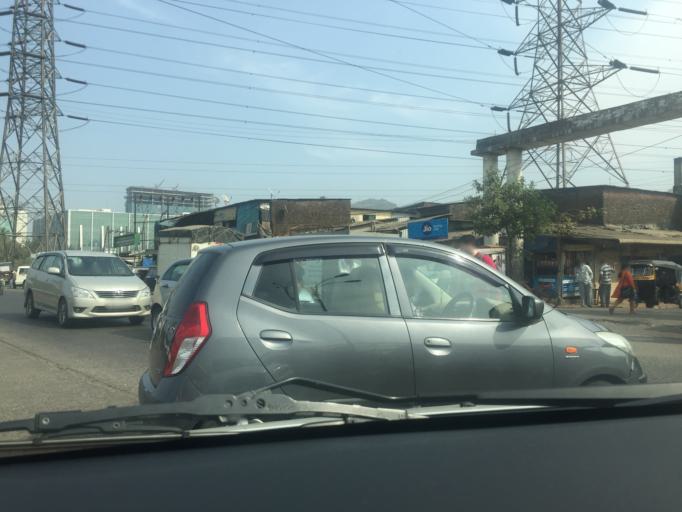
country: IN
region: Maharashtra
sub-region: Thane
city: Airoli
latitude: 19.1657
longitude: 72.9996
